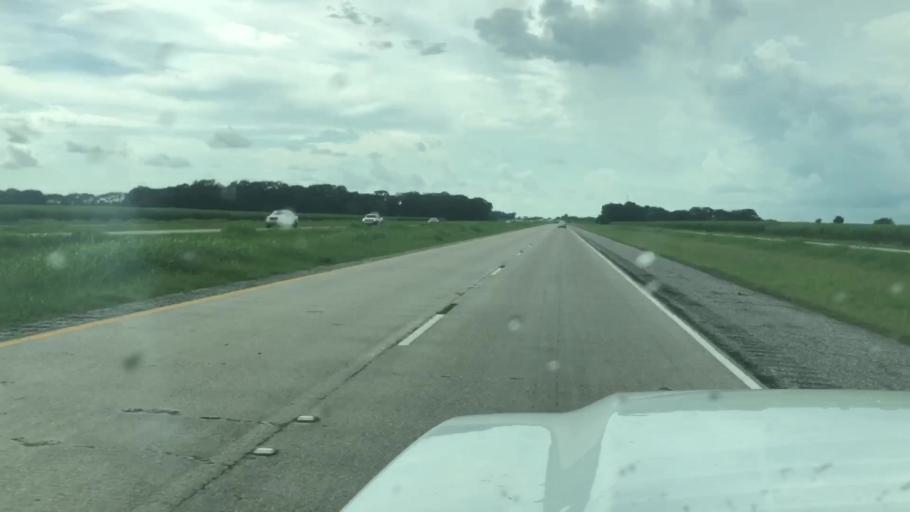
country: US
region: Louisiana
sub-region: Saint Mary Parish
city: Baldwin
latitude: 29.8540
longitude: -91.6046
